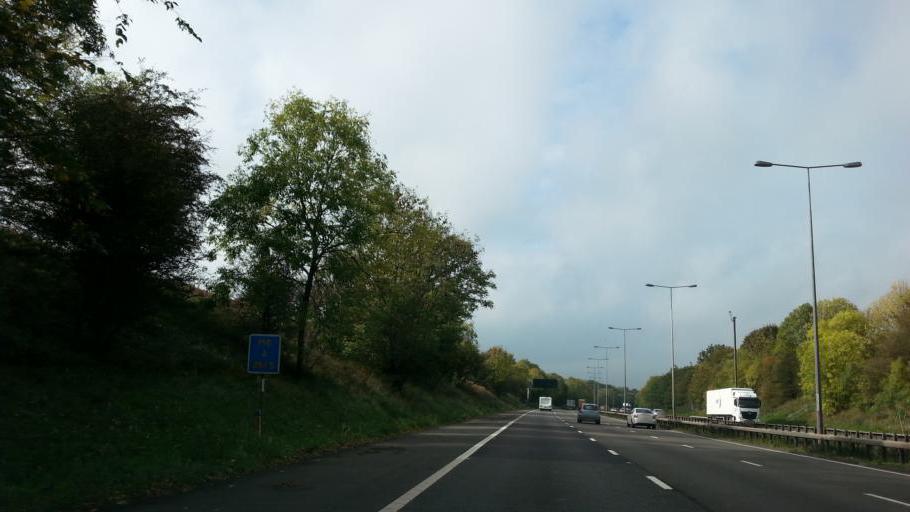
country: GB
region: England
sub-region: Staffordshire
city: Audley
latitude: 52.9937
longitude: -2.2968
